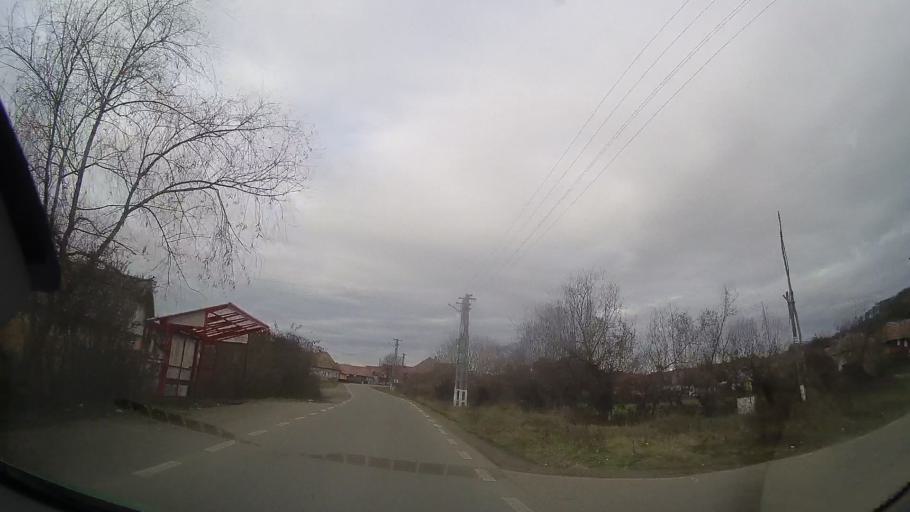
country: RO
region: Mures
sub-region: Comuna Faragau
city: Faragau
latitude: 46.7778
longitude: 24.5550
